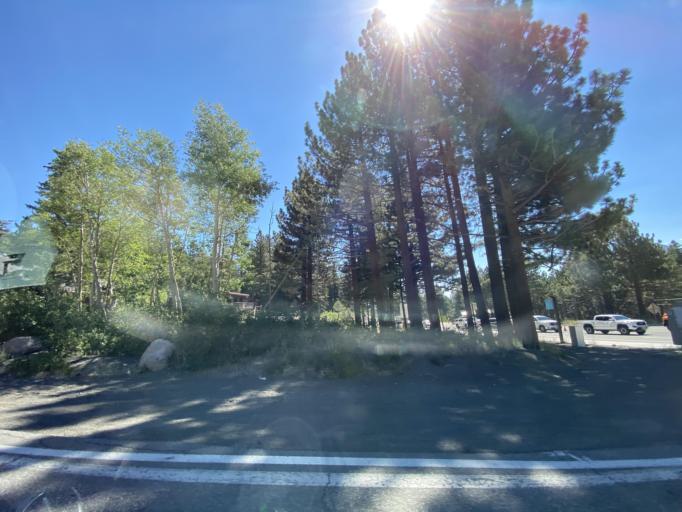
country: US
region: California
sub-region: Mono County
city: Mammoth Lakes
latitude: 37.6487
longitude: -118.9831
